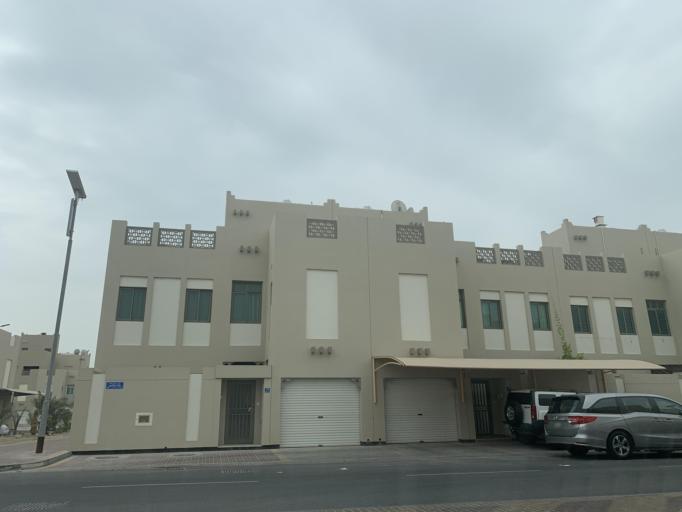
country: BH
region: Northern
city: Madinat `Isa
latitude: 26.1710
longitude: 50.5110
